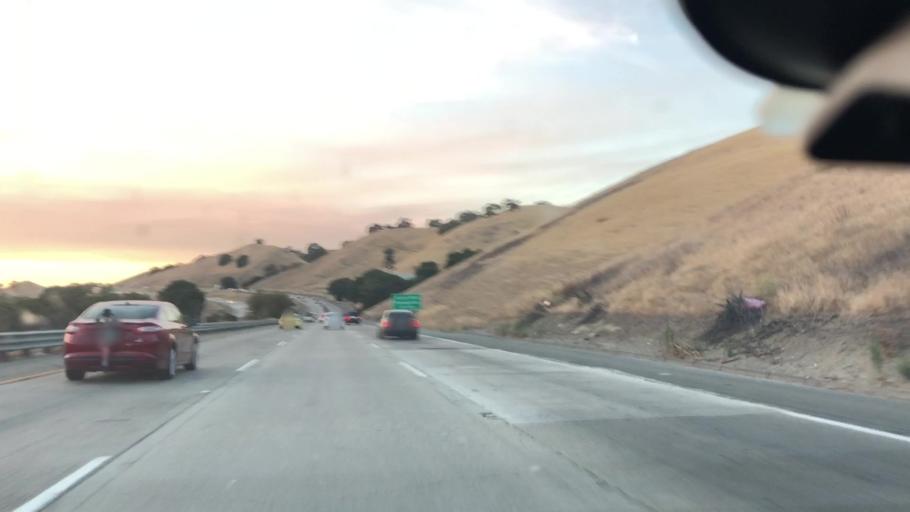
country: US
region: California
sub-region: Alameda County
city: Pleasanton
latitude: 37.6236
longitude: -121.8799
